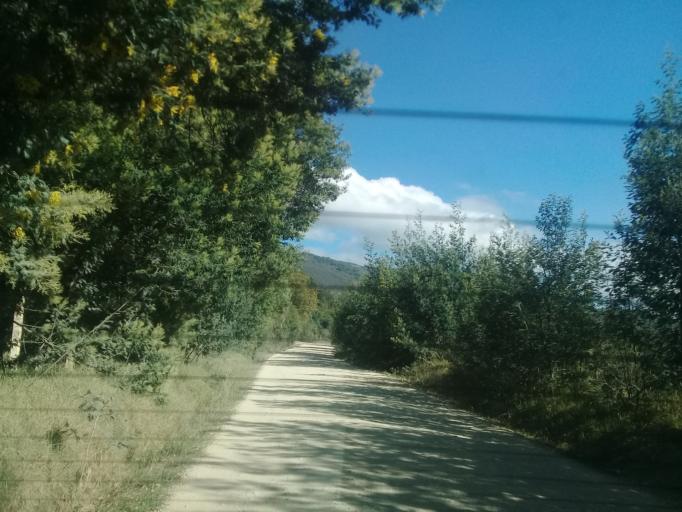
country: CO
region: Cundinamarca
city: Guasca
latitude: 4.9186
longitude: -73.8853
